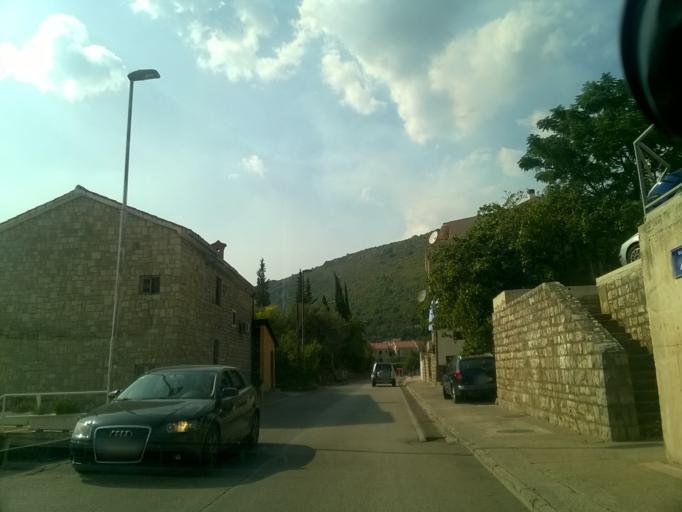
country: ME
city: Petrovac na Moru
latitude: 42.2065
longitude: 18.9472
